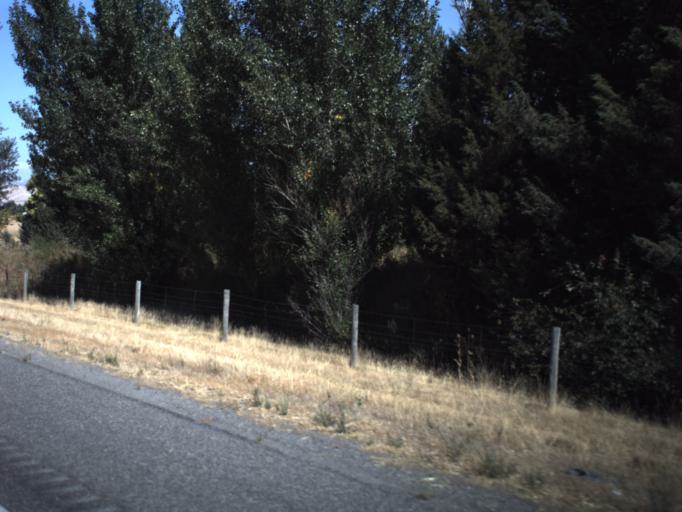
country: US
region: Utah
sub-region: Cache County
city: Richmond
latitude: 41.9554
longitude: -111.8130
